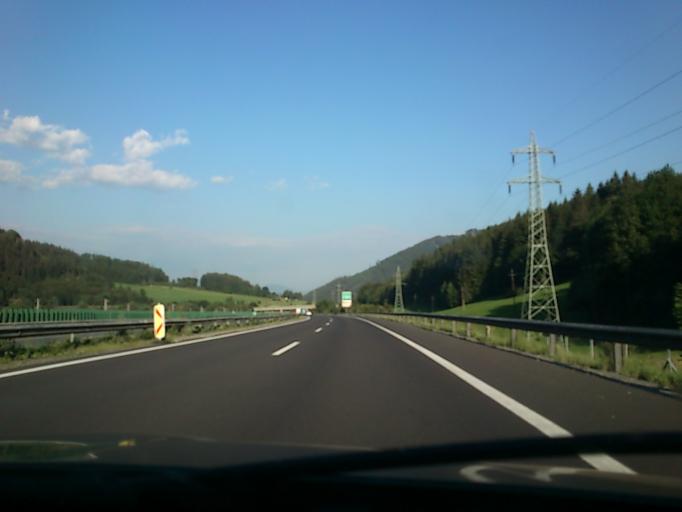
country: AT
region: Styria
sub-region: Politischer Bezirk Leoben
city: Kammern im Liesingtal
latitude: 47.3921
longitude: 14.8690
